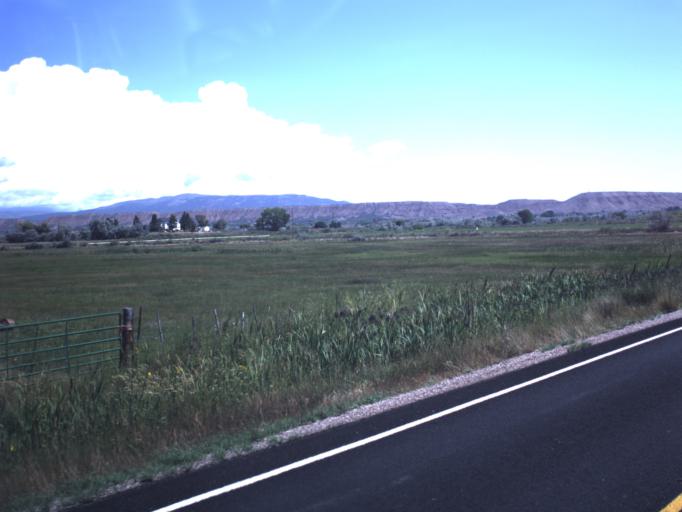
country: US
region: Utah
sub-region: Duchesne County
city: Roosevelt
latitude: 40.4037
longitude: -109.8574
